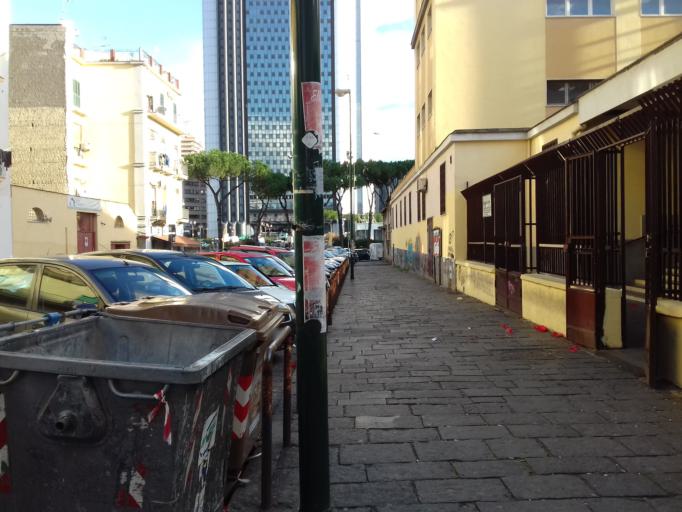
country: IT
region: Campania
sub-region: Provincia di Napoli
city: Napoli
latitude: 40.8571
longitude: 14.2754
